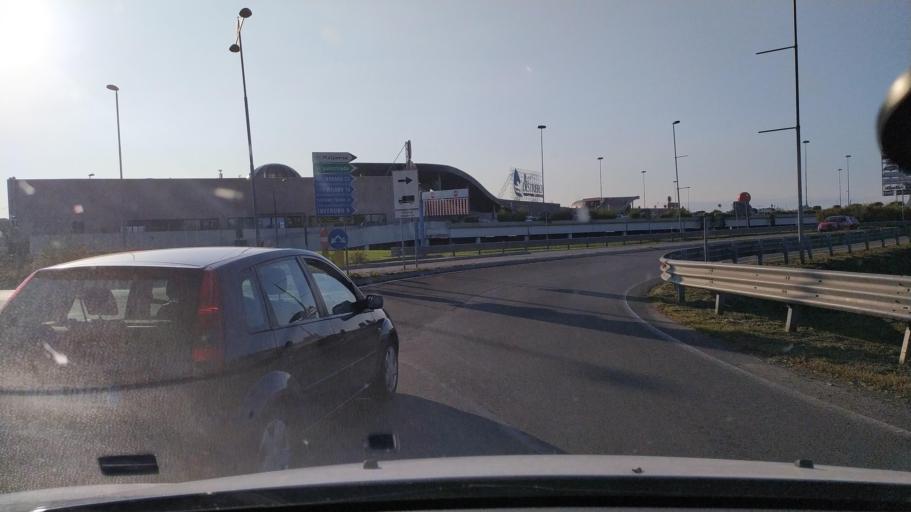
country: IT
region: Lombardy
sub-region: Citta metropolitana di Milano
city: Vittuone
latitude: 45.4795
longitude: 8.9508
